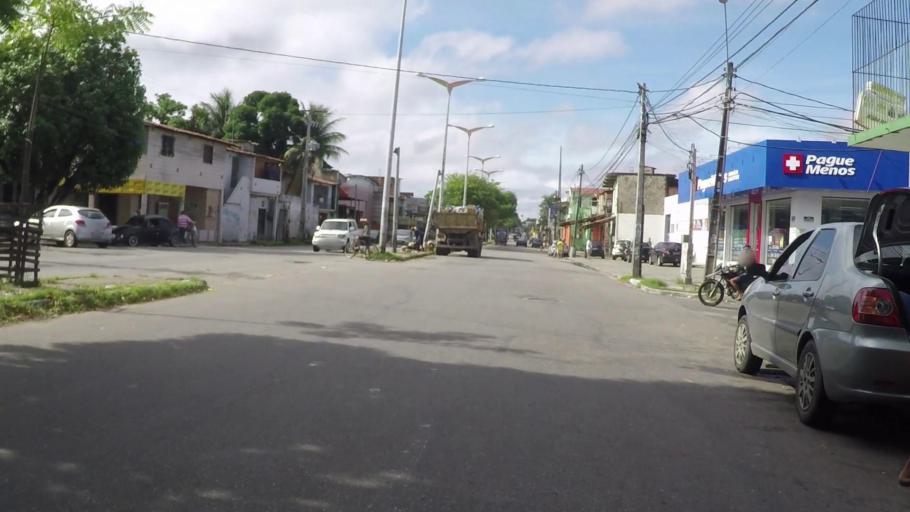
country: BR
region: Ceara
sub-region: Fortaleza
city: Fortaleza
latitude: -3.7205
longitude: -38.5873
